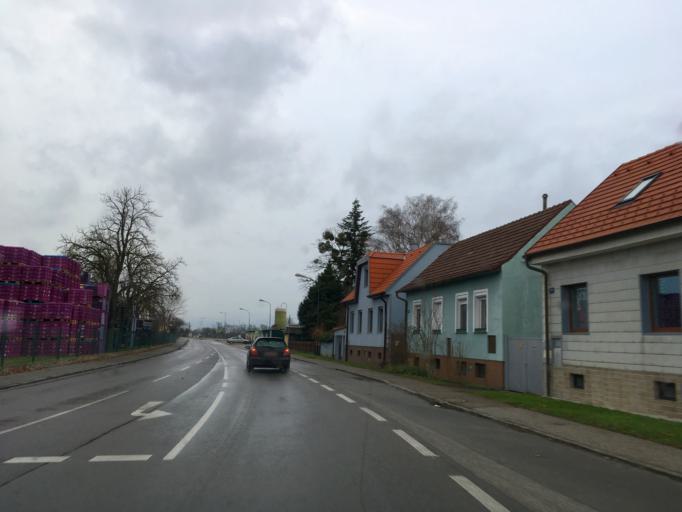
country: AT
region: Lower Austria
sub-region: Politischer Bezirk Wien-Umgebung
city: Ebergassing
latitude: 48.0437
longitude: 16.5215
